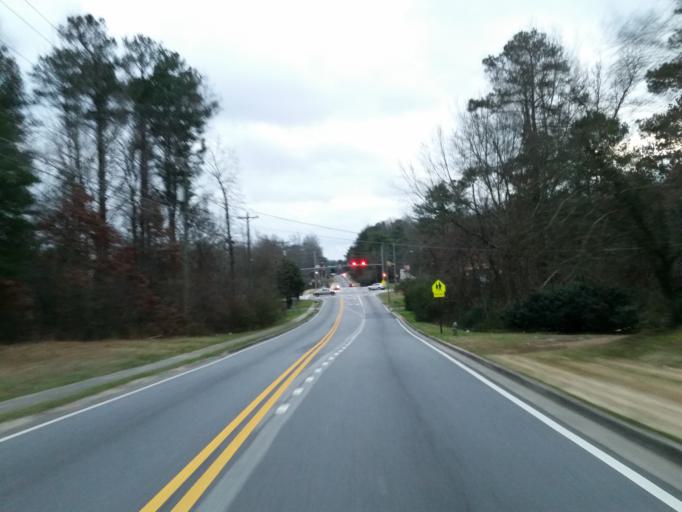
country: US
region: Georgia
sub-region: Cobb County
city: Fair Oaks
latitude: 33.8826
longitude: -84.5797
